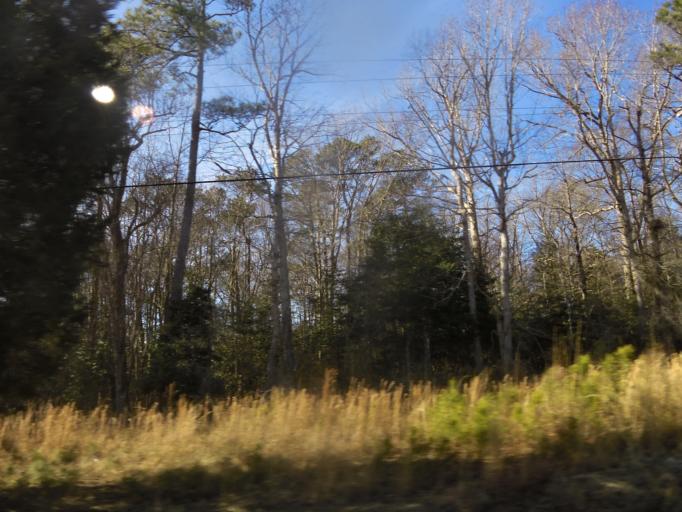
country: US
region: Virginia
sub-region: Isle of Wight County
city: Isle of Wight
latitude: 36.9249
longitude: -76.6886
